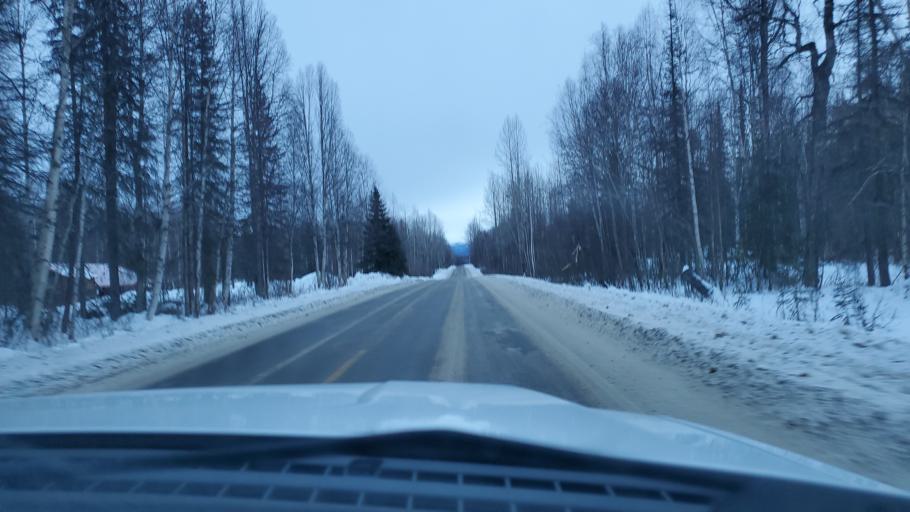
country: US
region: Alaska
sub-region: Matanuska-Susitna Borough
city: Y
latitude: 62.3163
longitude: -150.2479
